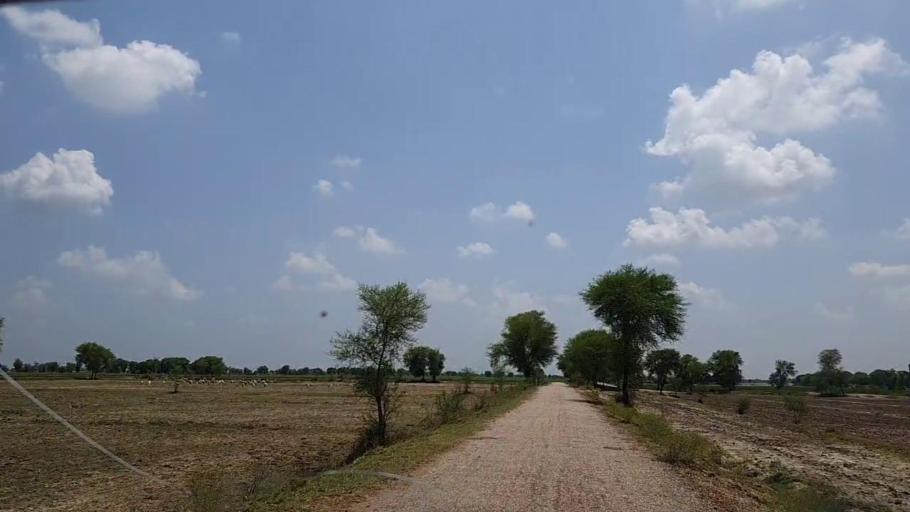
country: PK
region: Sindh
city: Tharu Shah
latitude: 27.0190
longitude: 68.0721
